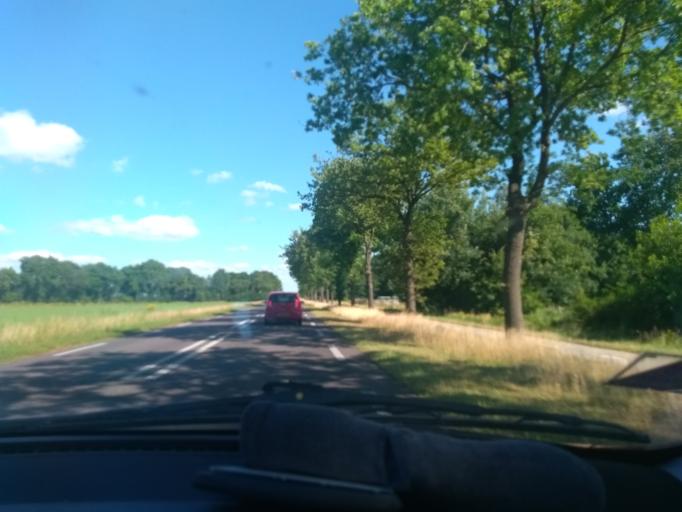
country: NL
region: Drenthe
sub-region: Gemeente Tynaarlo
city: Vries
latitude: 53.1056
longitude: 6.5304
